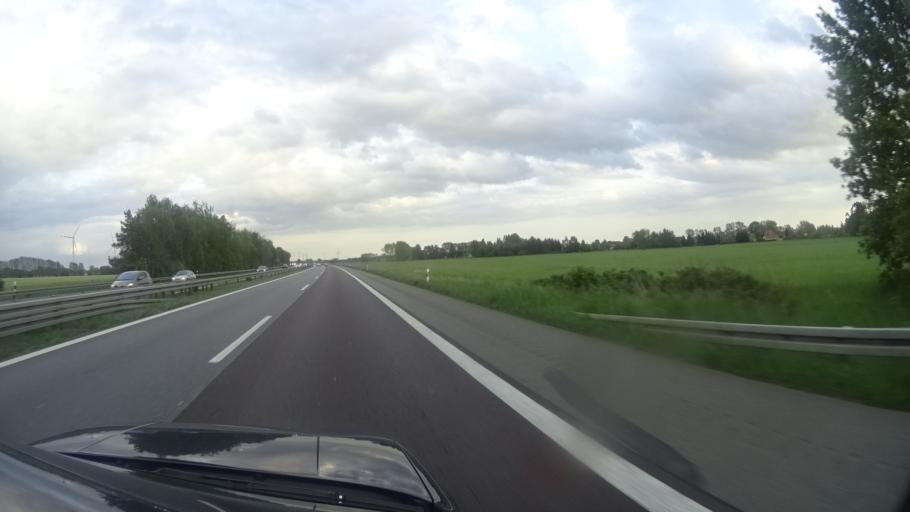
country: DE
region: Brandenburg
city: Walsleben
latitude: 52.9436
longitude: 12.6714
